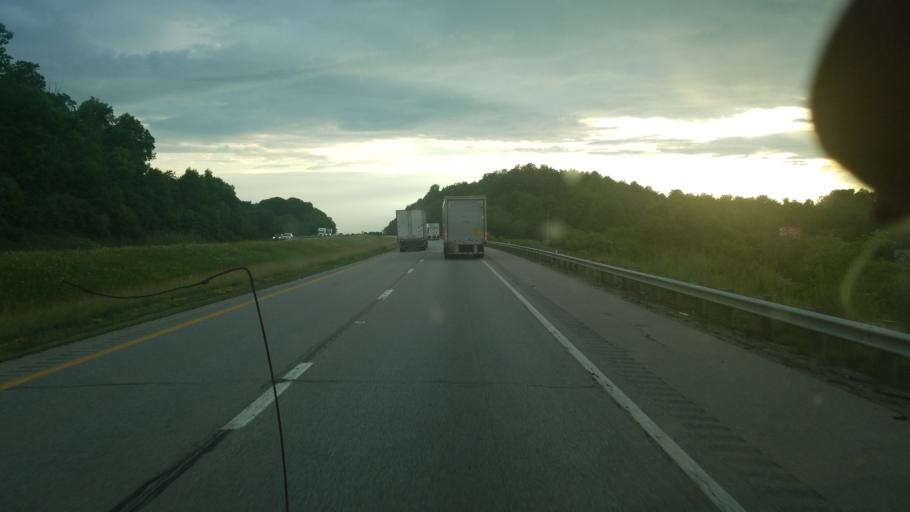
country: US
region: Ohio
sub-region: Muskingum County
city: New Concord
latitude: 39.9789
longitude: -81.7653
